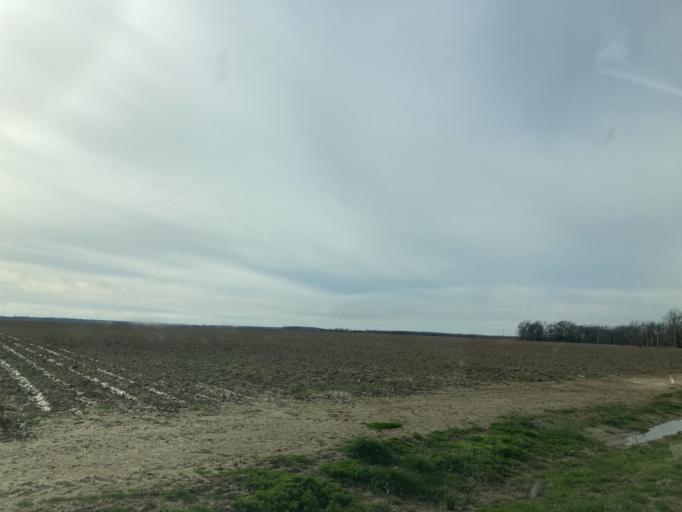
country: US
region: Mississippi
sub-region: Humphreys County
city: Belzoni
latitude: 33.1164
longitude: -90.6149
